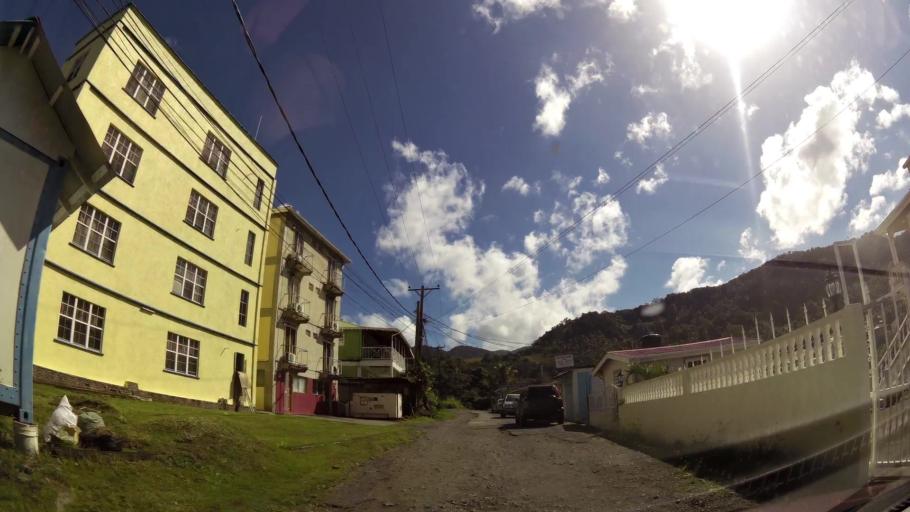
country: DM
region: Saint John
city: Portsmouth
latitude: 15.5535
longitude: -61.4602
